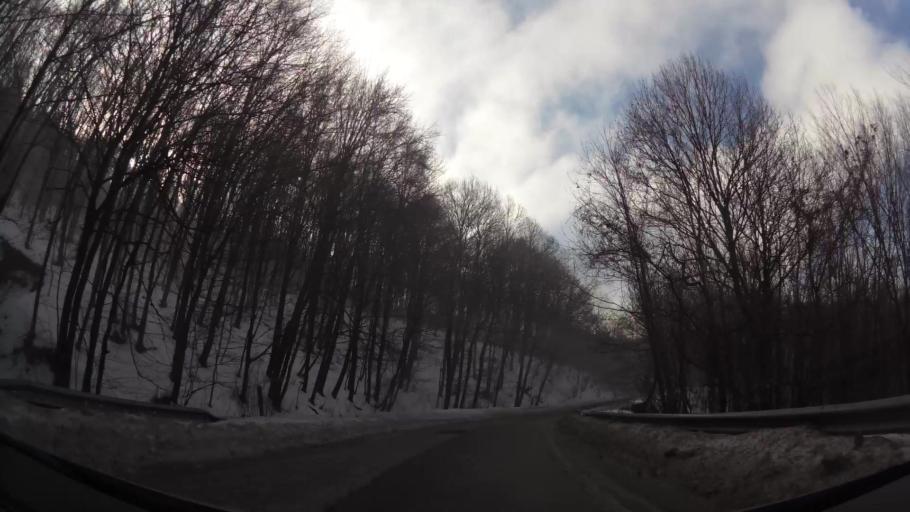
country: BG
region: Sofiya
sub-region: Obshtina Bozhurishte
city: Bozhurishte
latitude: 42.6424
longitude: 23.2232
